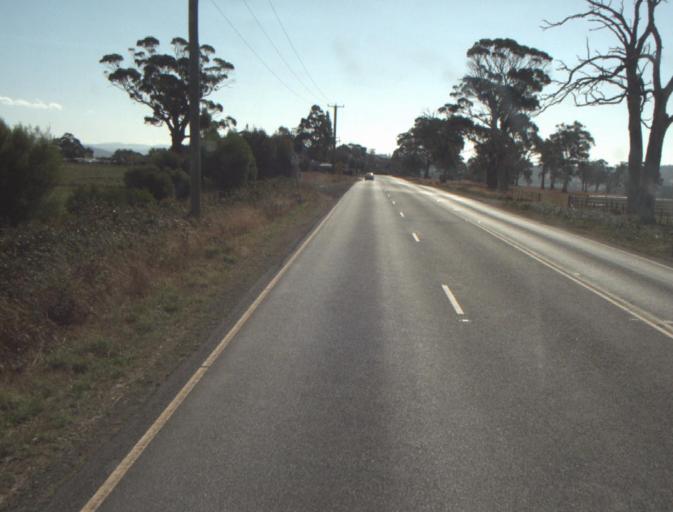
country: AU
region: Tasmania
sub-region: Launceston
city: Mayfield
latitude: -41.3419
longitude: 147.0894
